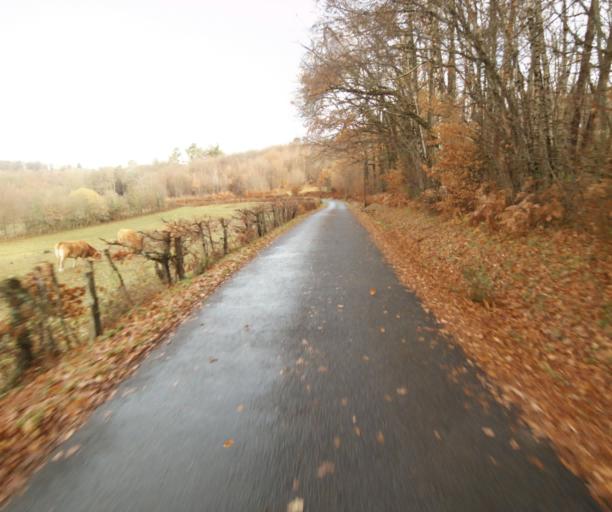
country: FR
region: Limousin
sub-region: Departement de la Correze
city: Saint-Mexant
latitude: 45.2523
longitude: 1.6451
